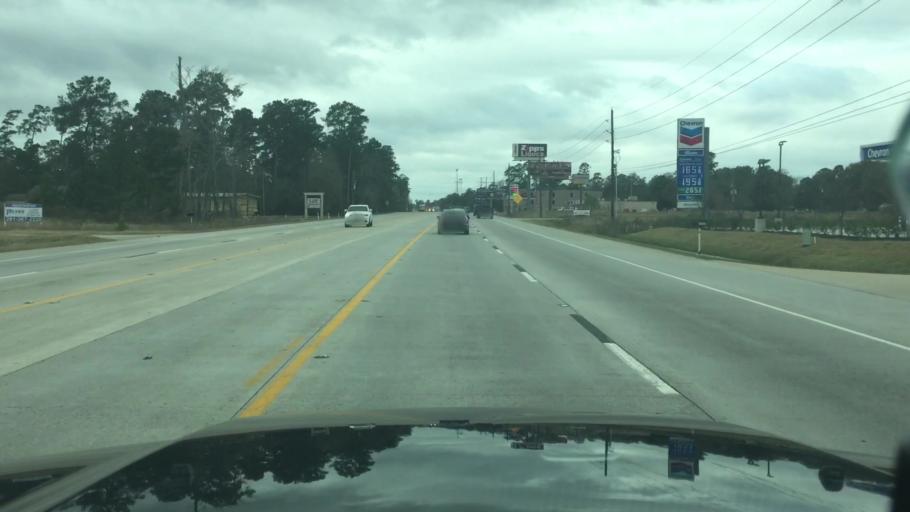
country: US
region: Texas
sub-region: Montgomery County
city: Shenandoah
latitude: 30.2310
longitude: -95.5024
